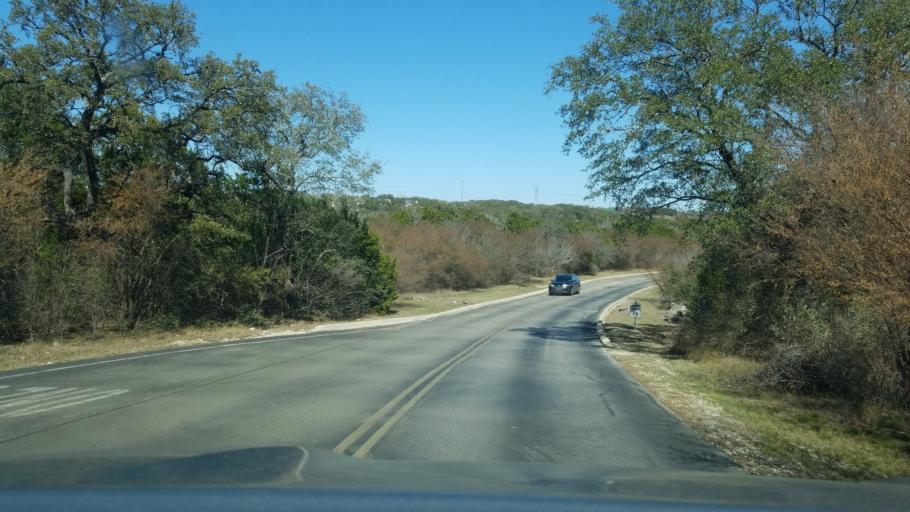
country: US
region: Texas
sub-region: Bexar County
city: Hollywood Park
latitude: 29.6074
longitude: -98.4569
